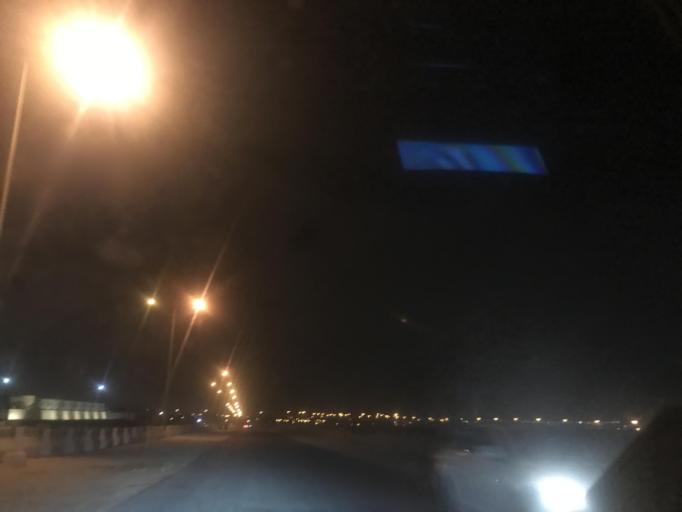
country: SA
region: Ar Riyad
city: Riyadh
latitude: 24.7635
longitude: 46.5881
